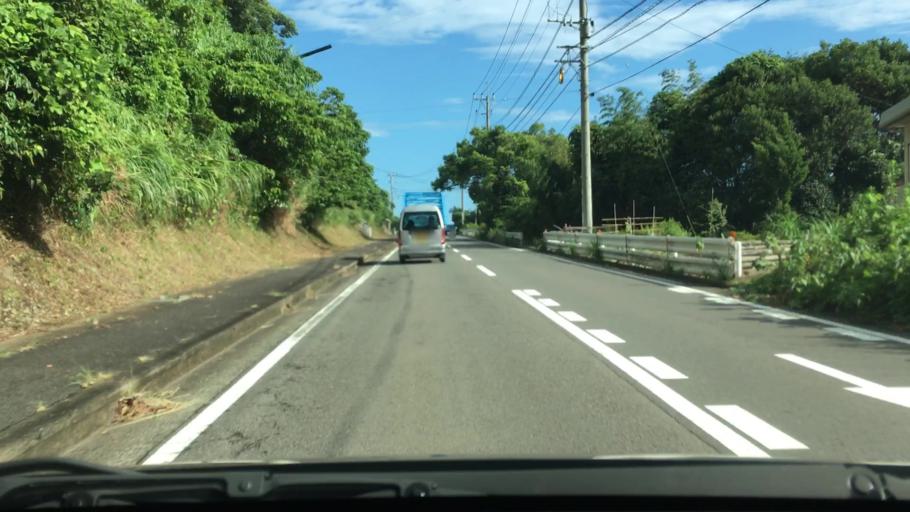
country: JP
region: Nagasaki
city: Togitsu
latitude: 32.8534
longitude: 129.6893
